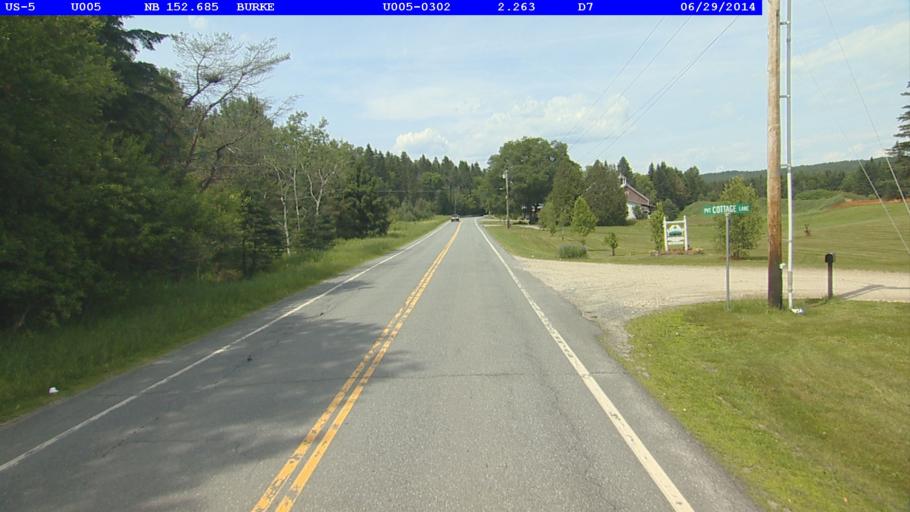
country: US
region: Vermont
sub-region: Caledonia County
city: Lyndonville
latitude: 44.6173
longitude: -71.9722
